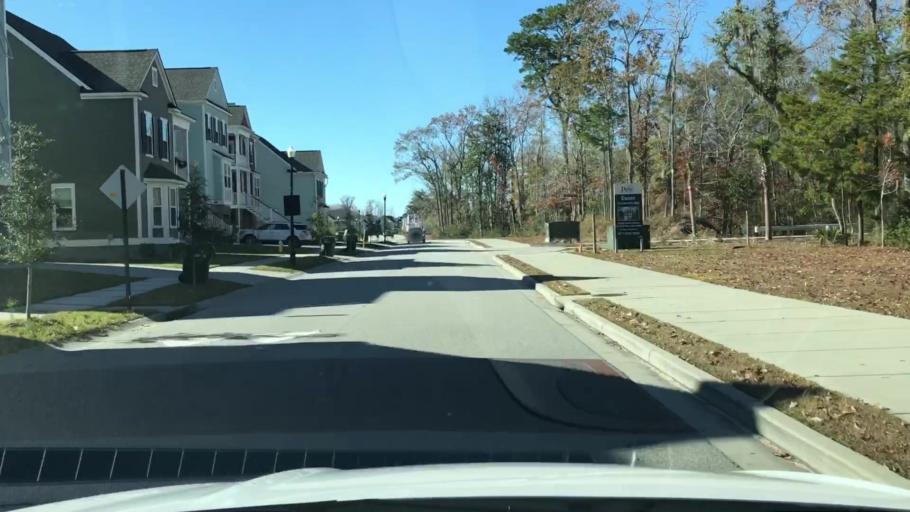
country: US
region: South Carolina
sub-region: Charleston County
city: Shell Point
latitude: 32.8085
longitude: -80.0621
